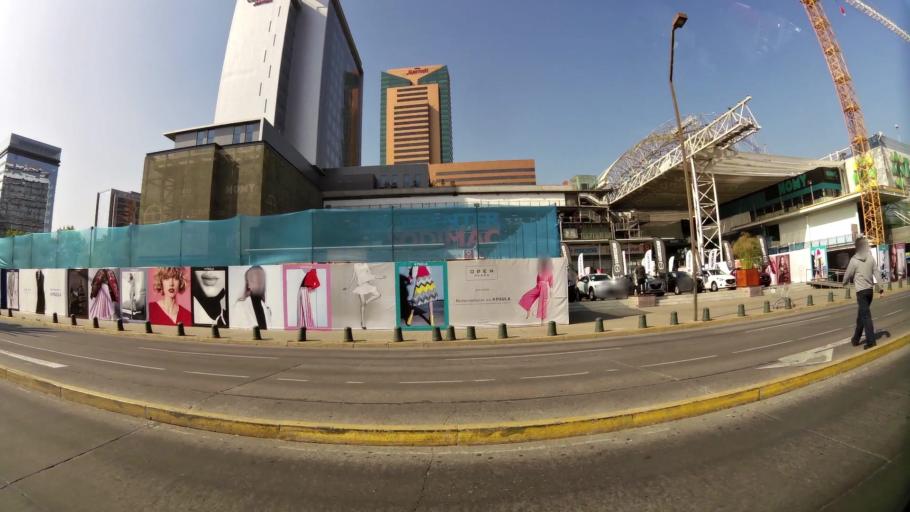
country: CL
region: Santiago Metropolitan
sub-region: Provincia de Santiago
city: Villa Presidente Frei, Nunoa, Santiago, Chile
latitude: -33.4012
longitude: -70.5765
